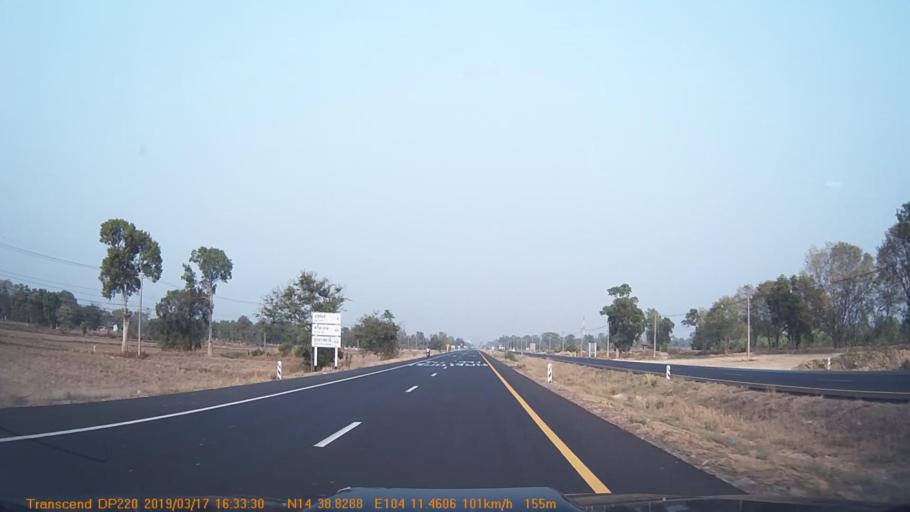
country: TH
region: Sisaket
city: Khu Khan
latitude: 14.6472
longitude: 104.1912
